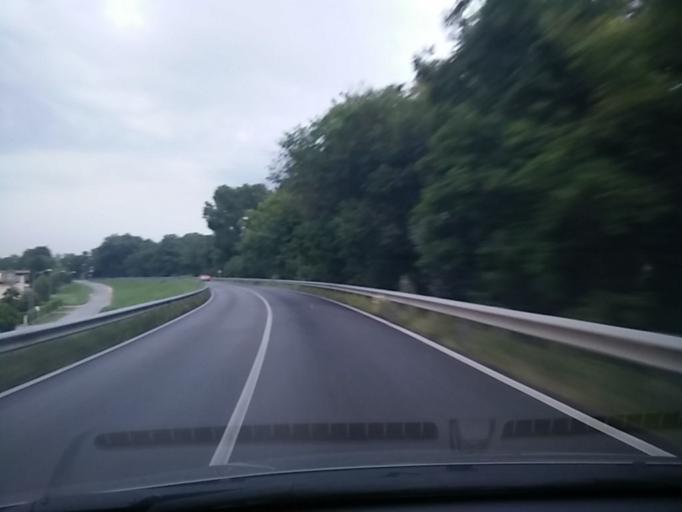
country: IT
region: Veneto
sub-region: Provincia di Venezia
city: San Dona di Piave
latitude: 45.6187
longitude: 12.5732
